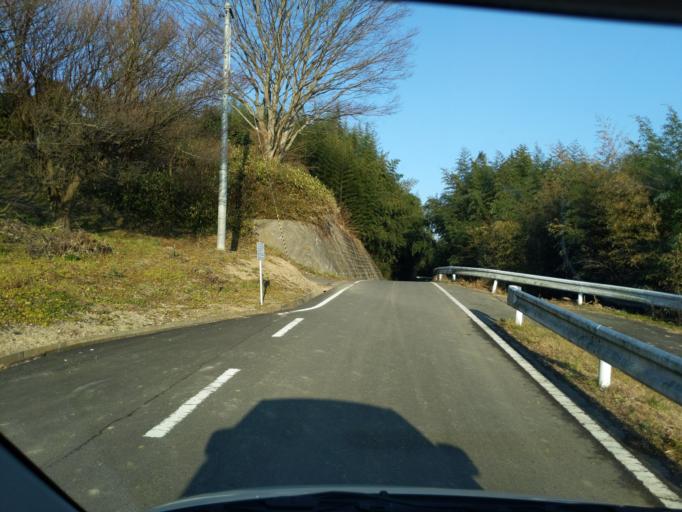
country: JP
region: Miyagi
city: Wakuya
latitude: 38.7063
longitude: 141.1389
